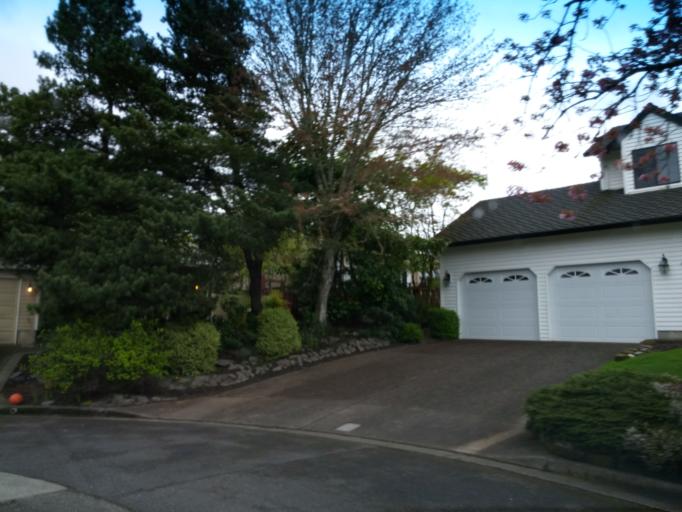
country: US
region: Oregon
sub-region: Washington County
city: Oak Hills
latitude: 45.5263
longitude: -122.8430
